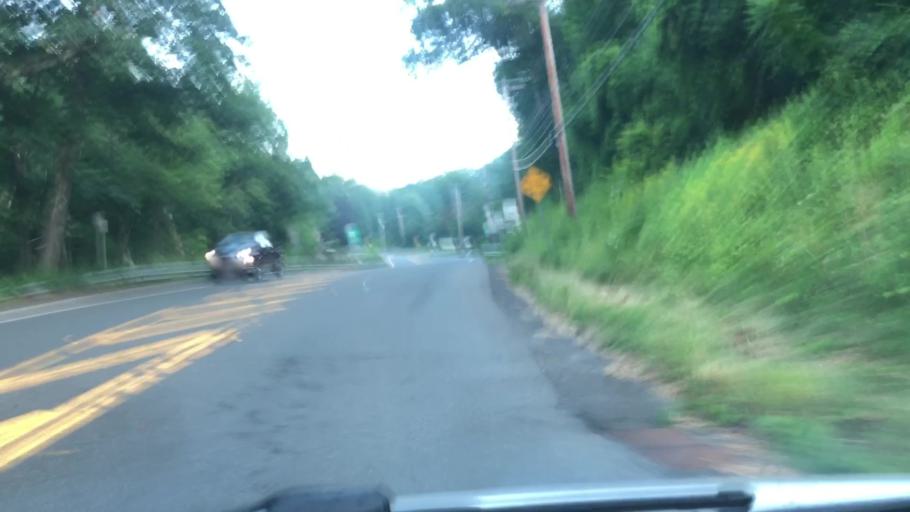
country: US
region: Massachusetts
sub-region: Hampshire County
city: Williamsburg
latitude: 42.3941
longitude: -72.7360
